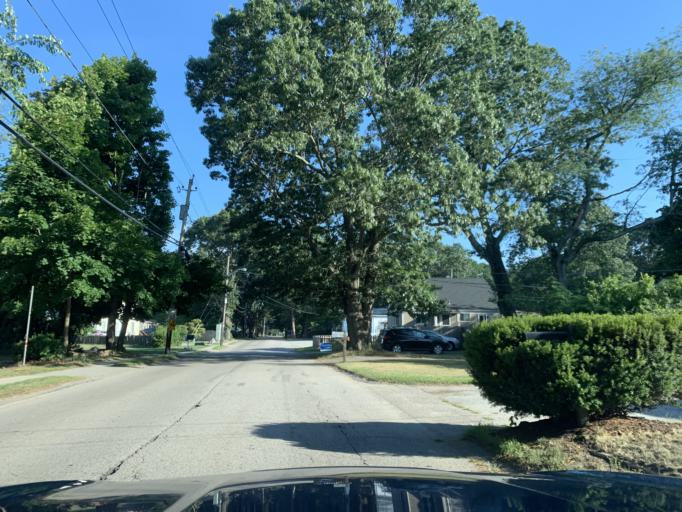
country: US
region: Rhode Island
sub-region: Kent County
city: Warwick
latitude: 41.6961
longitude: -71.4397
